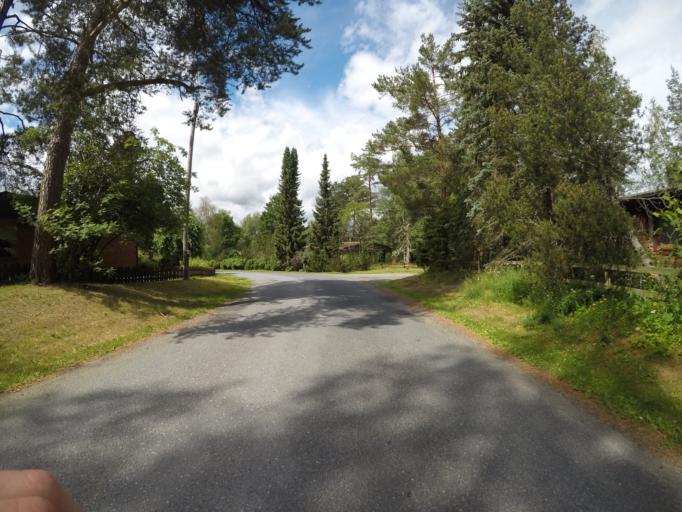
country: FI
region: Haeme
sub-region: Haemeenlinna
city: Haemeenlinna
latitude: 60.9735
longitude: 24.4338
